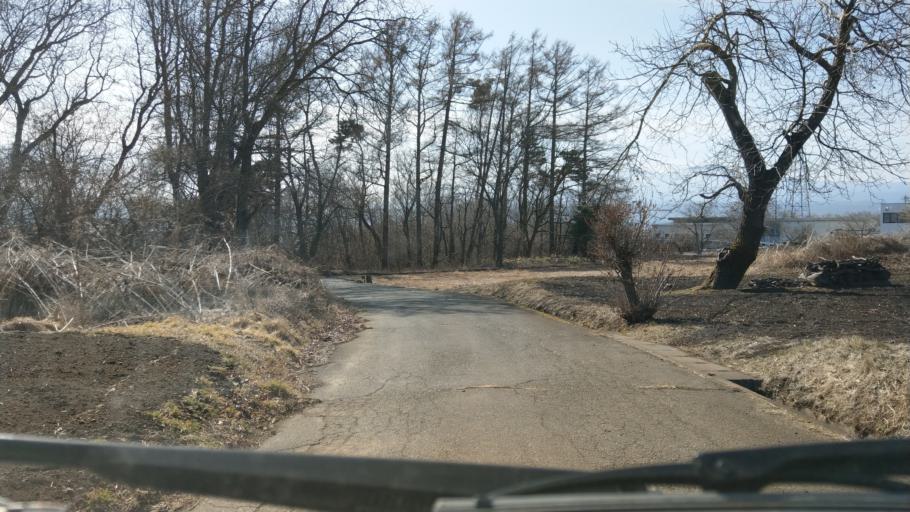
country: JP
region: Nagano
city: Komoro
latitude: 36.3186
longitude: 138.4491
